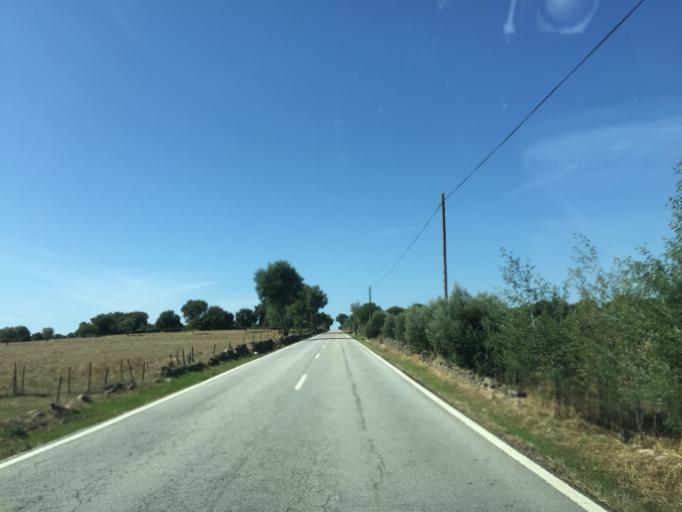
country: PT
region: Portalegre
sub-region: Portalegre
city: Alagoa
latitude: 39.4244
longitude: -7.5948
